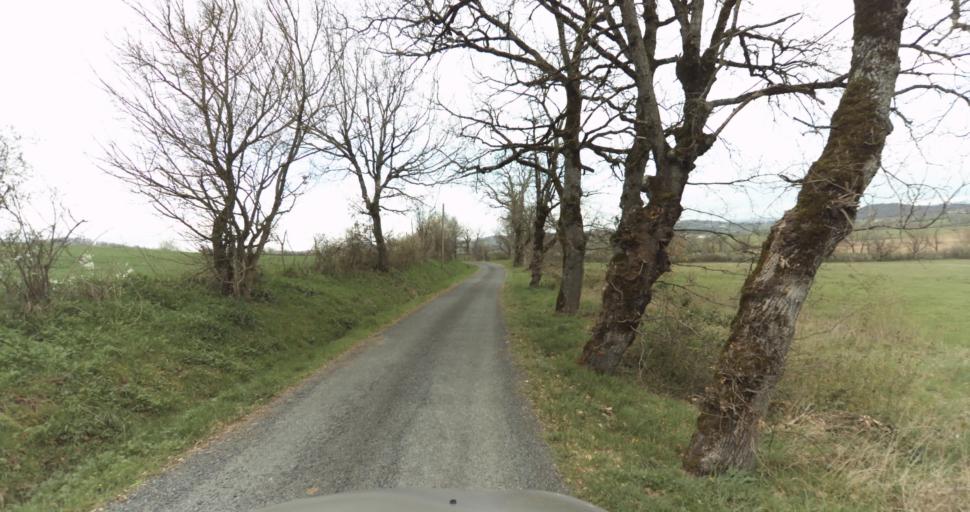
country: FR
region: Midi-Pyrenees
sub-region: Departement du Tarn
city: Frejairolles
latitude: 43.8696
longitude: 2.2099
